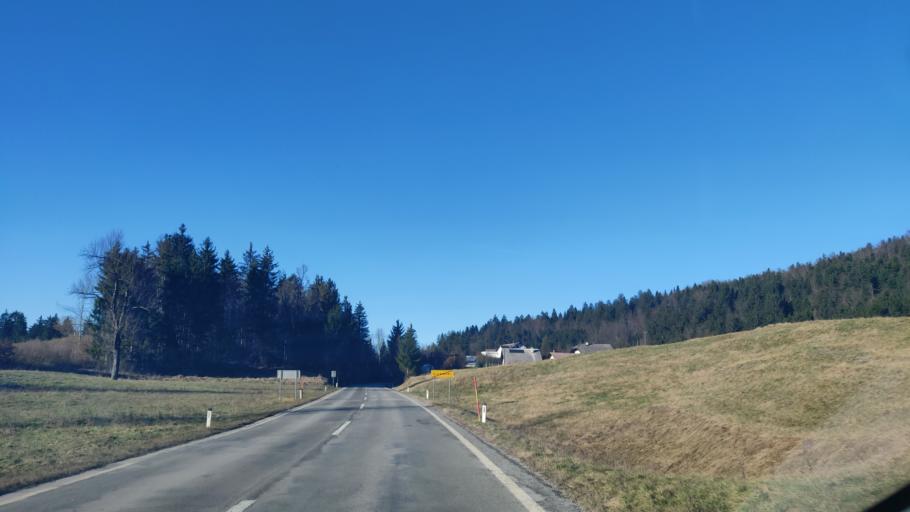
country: SI
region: Logatec
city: Logatec
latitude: 45.8756
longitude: 14.2116
